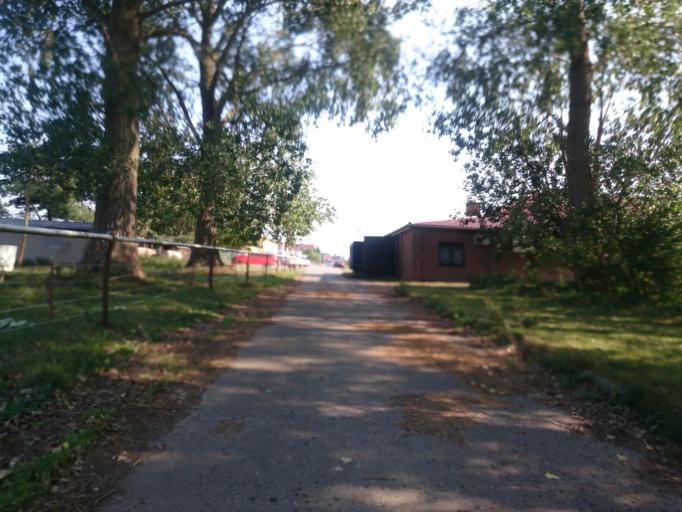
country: DE
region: Mecklenburg-Vorpommern
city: Barth
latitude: 54.3627
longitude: 12.7112
